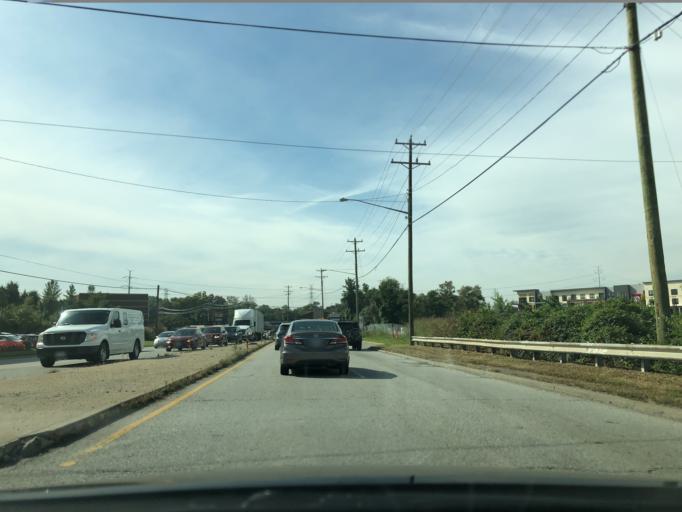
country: US
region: Ohio
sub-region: Hamilton County
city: Fairfax
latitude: 39.1602
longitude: -84.4046
